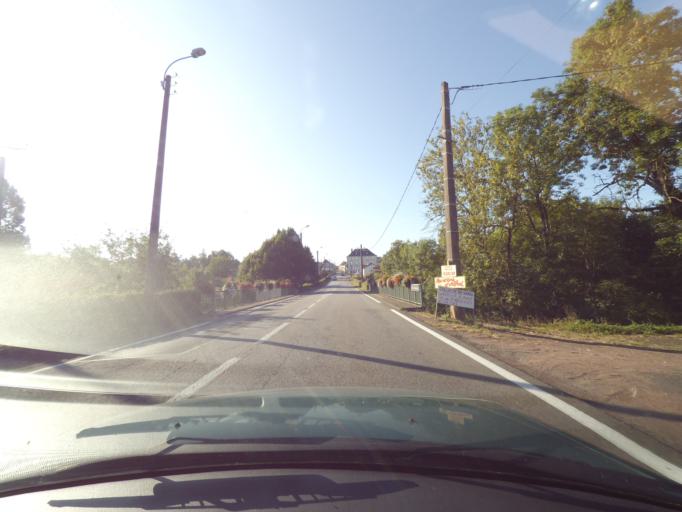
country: FR
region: Poitou-Charentes
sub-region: Departement des Deux-Sevres
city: Chiche
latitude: 46.7992
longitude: -0.3620
